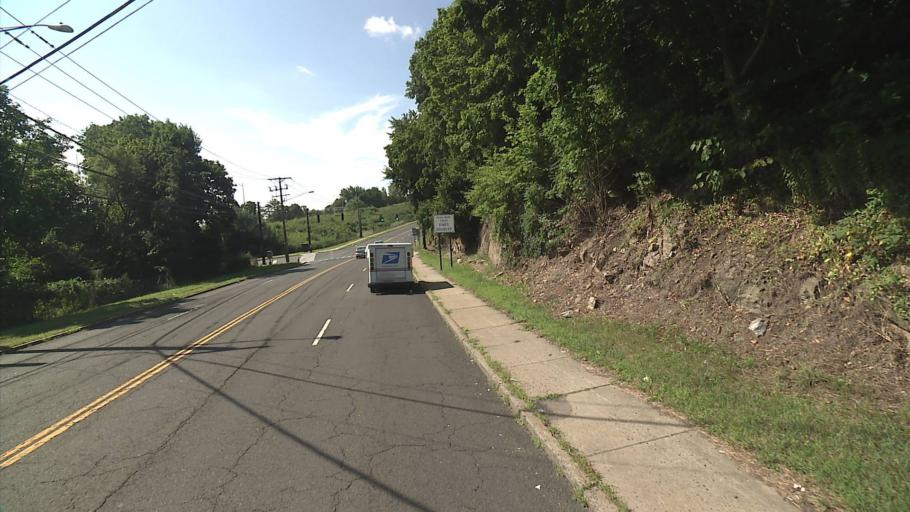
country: US
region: Connecticut
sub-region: Fairfield County
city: Norwalk
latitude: 41.1105
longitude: -73.4197
